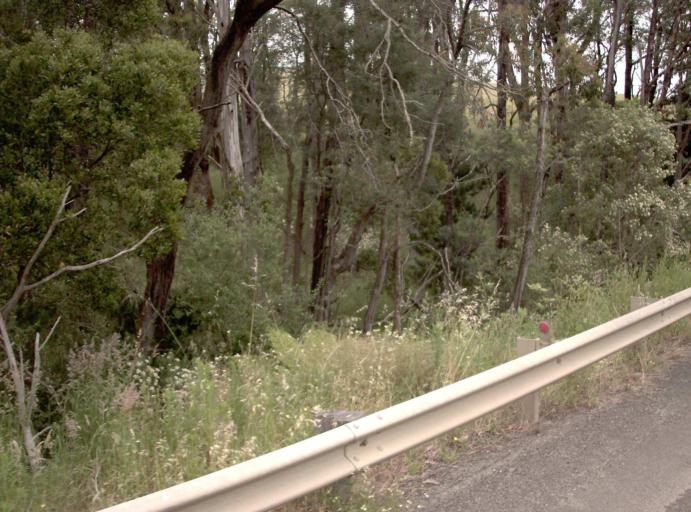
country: AU
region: Victoria
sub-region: Latrobe
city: Moe
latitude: -38.3844
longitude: 146.1728
